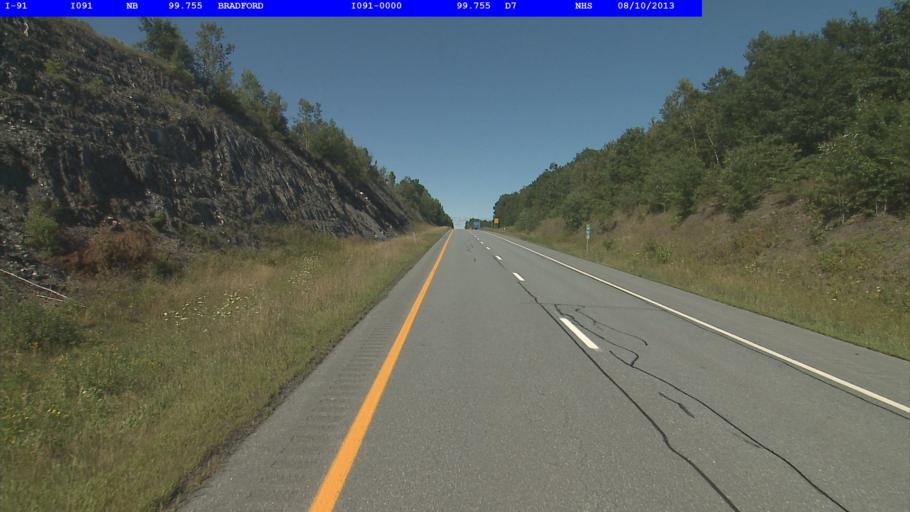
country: US
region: New Hampshire
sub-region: Grafton County
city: Haverhill
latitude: 44.0119
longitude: -72.1231
